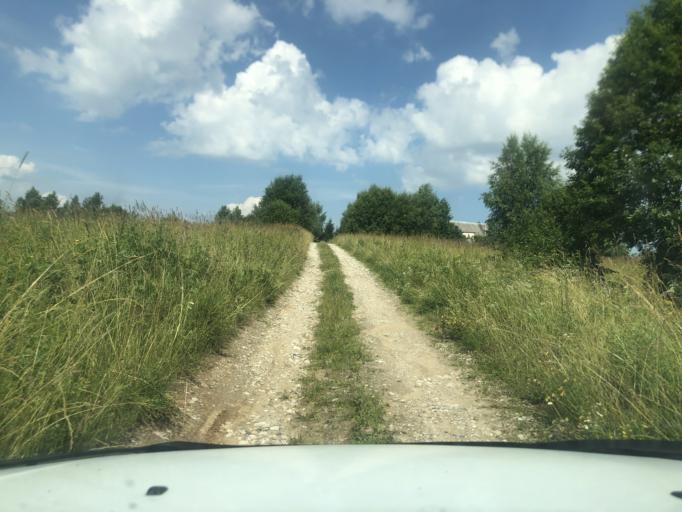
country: RU
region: Jaroslavl
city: Pereslavl'-Zalesskiy
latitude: 57.0446
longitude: 38.8733
